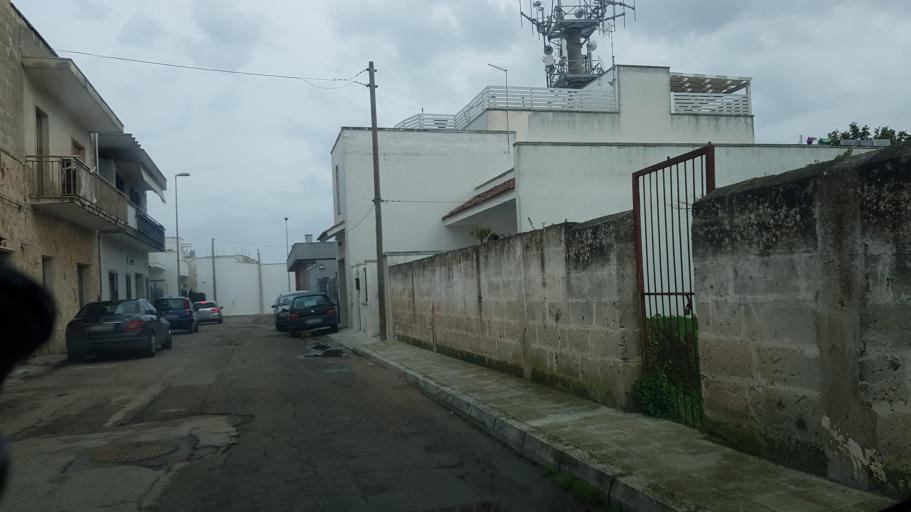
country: IT
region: Apulia
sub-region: Provincia di Lecce
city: Squinzano
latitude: 40.4359
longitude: 18.0377
